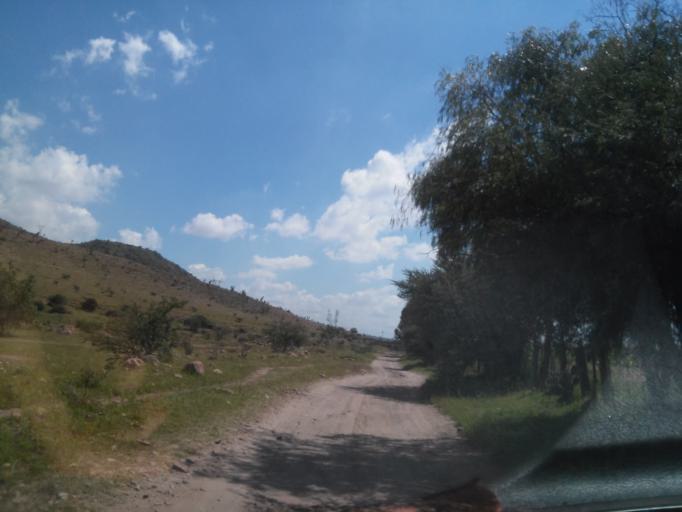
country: MX
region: Durango
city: Victoria de Durango
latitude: 24.0130
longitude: -104.7455
